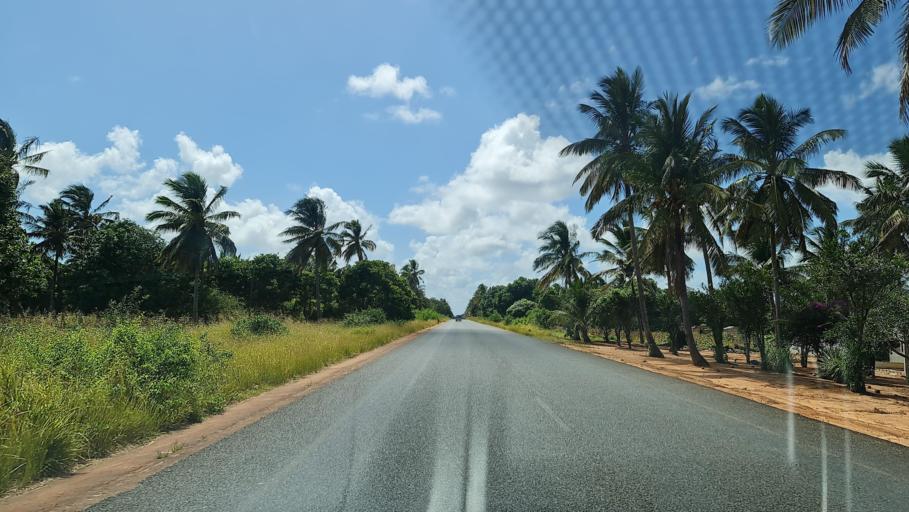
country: MZ
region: Inhambane
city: Maxixe
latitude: -24.5426
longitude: 34.8954
